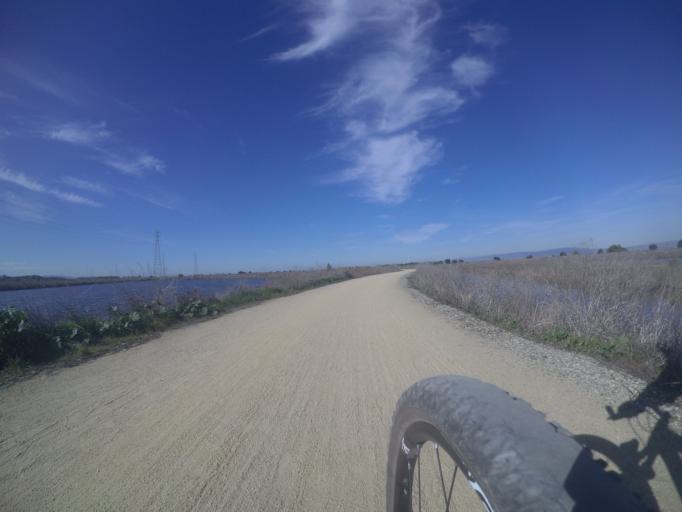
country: US
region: California
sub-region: Santa Clara County
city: Sunnyvale
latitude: 37.4238
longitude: -122.0272
